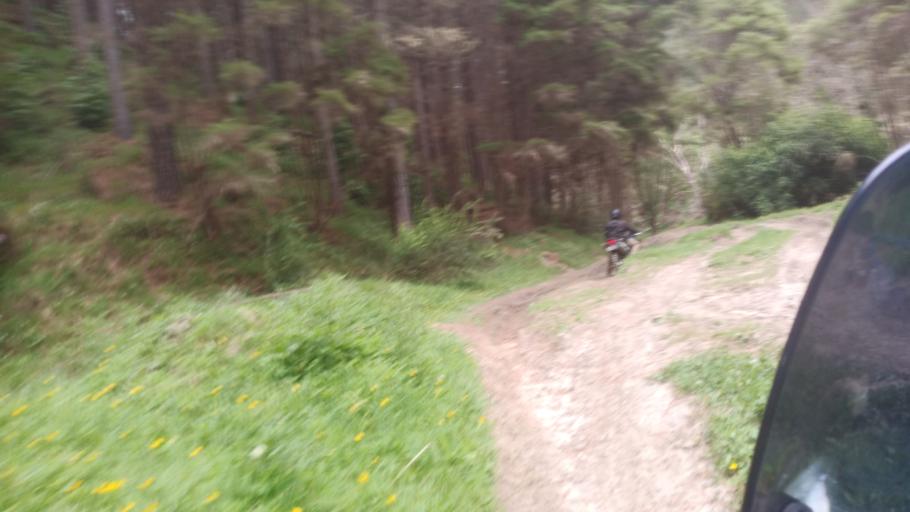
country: NZ
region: Gisborne
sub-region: Gisborne District
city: Gisborne
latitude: -38.4573
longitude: 177.9297
